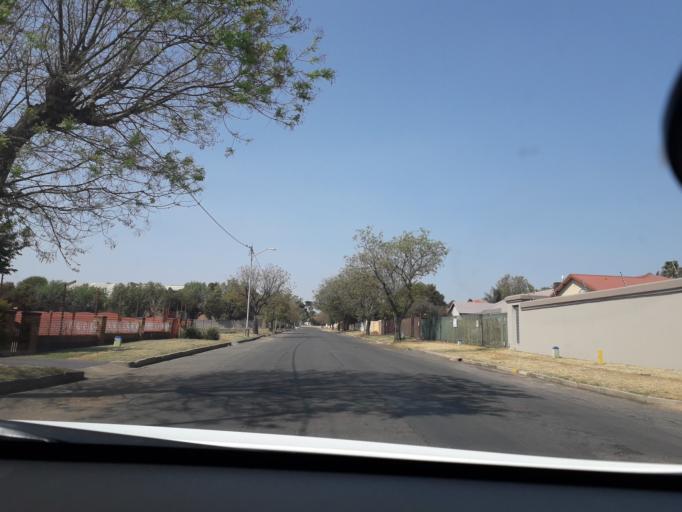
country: ZA
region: Gauteng
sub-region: City of Johannesburg Metropolitan Municipality
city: Modderfontein
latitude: -26.0936
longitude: 28.2268
